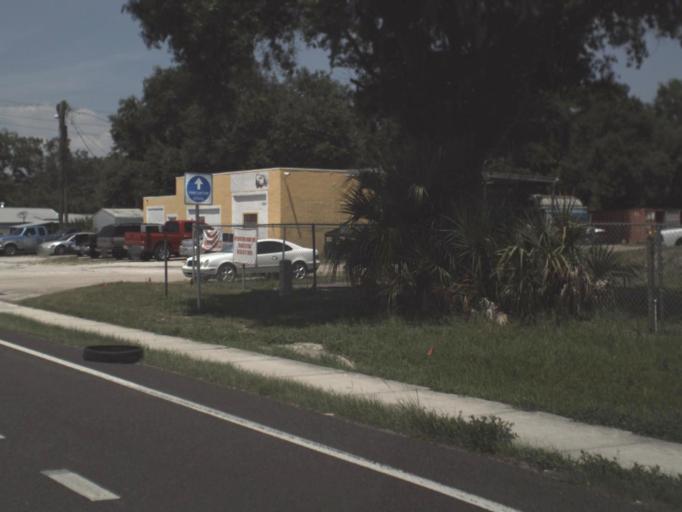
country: US
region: Florida
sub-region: Hillsborough County
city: Gibsonton
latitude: 27.8341
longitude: -82.3816
